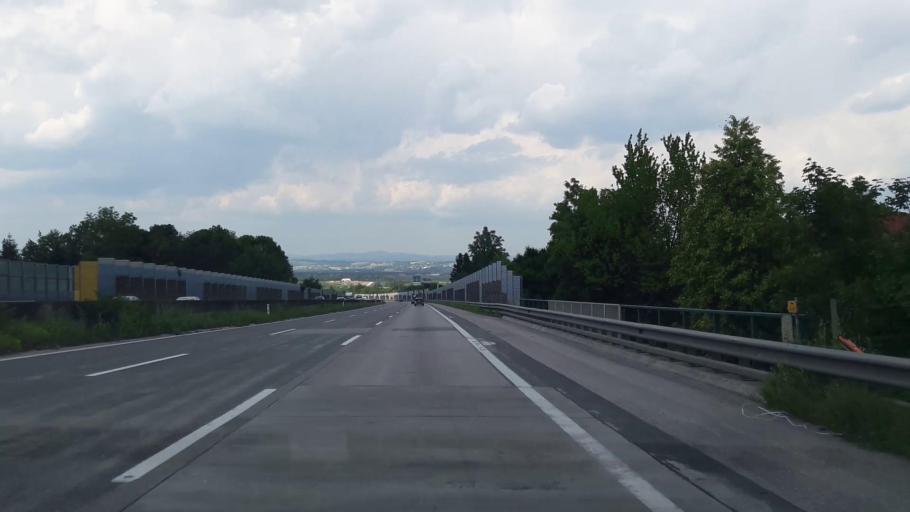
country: AT
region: Lower Austria
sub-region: Politischer Bezirk Amstetten
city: Sankt Valentin
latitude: 48.1725
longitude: 14.5483
